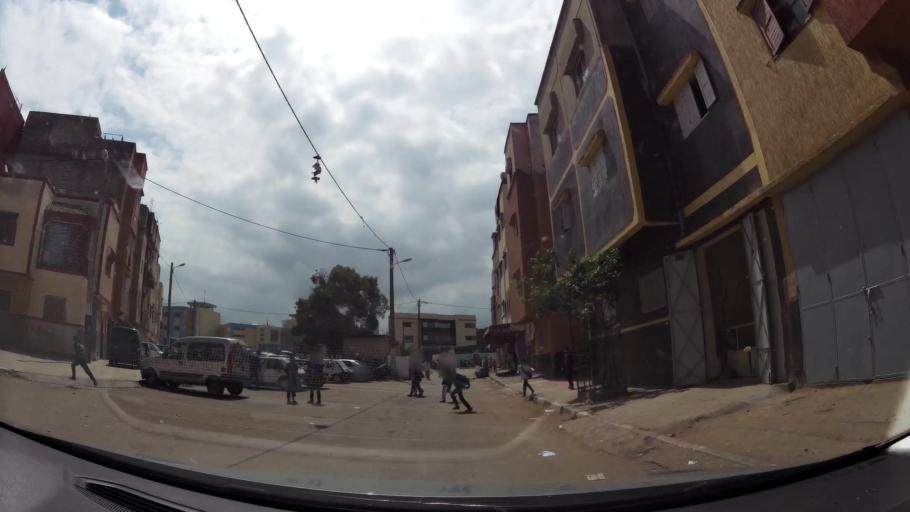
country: MA
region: Rabat-Sale-Zemmour-Zaer
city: Sale
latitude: 34.0666
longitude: -6.7822
